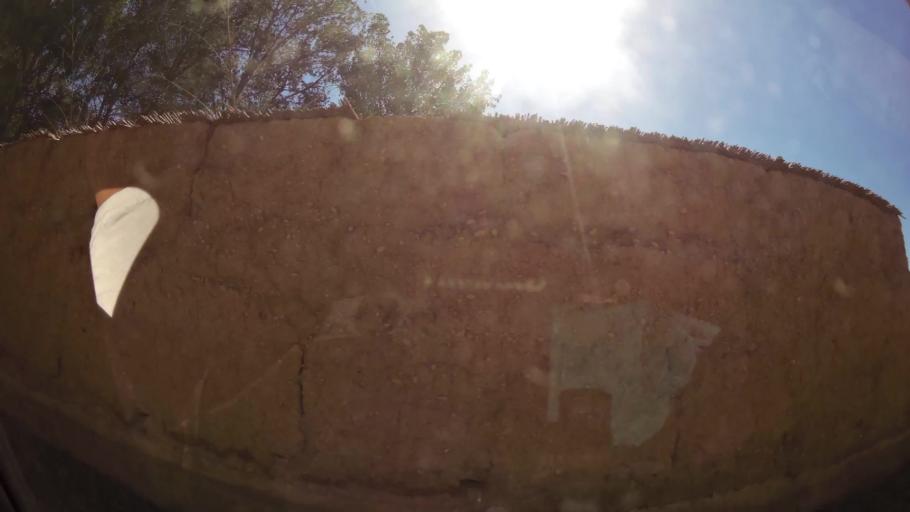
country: MA
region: Marrakech-Tensift-Al Haouz
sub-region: Marrakech
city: Marrakesh
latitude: 31.6669
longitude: -7.9600
